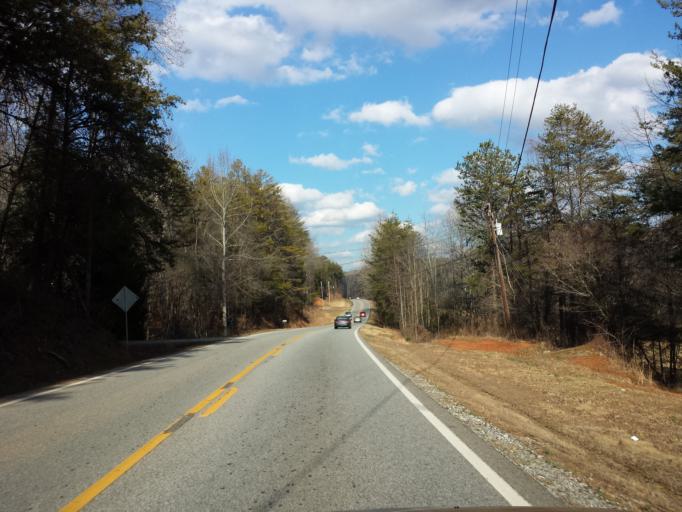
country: US
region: Georgia
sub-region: Lumpkin County
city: Dahlonega
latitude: 34.5009
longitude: -83.9370
